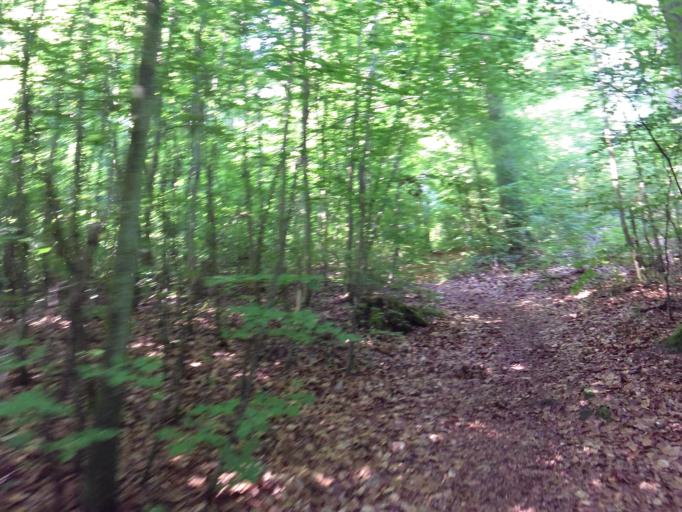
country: DE
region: Bavaria
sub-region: Regierungsbezirk Unterfranken
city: Reichenberg
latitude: 49.7639
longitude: 9.9109
